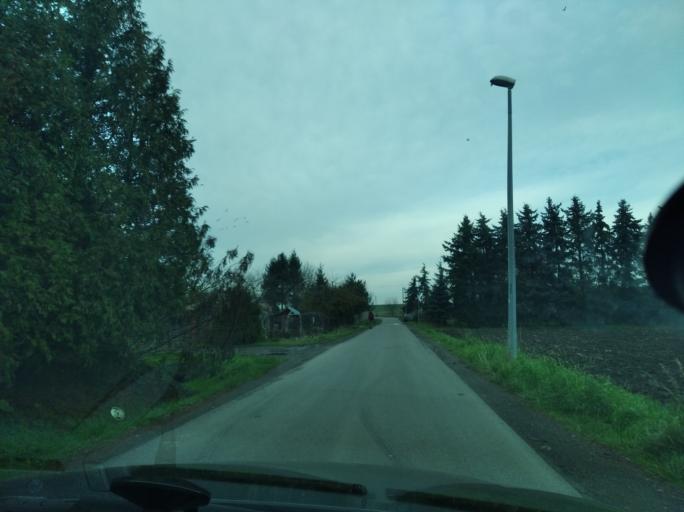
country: PL
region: Subcarpathian Voivodeship
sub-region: Powiat przeworski
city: Przeworsk
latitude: 50.0626
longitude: 22.4735
